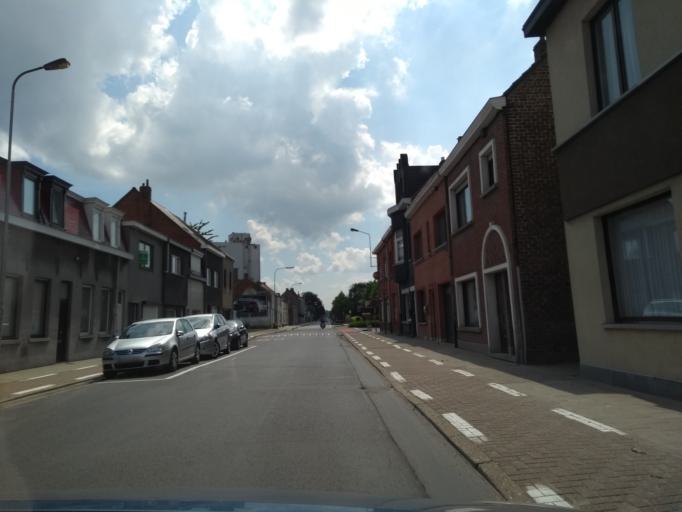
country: BE
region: Flanders
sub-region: Provincie Oost-Vlaanderen
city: Eeklo
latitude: 51.1821
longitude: 3.5538
